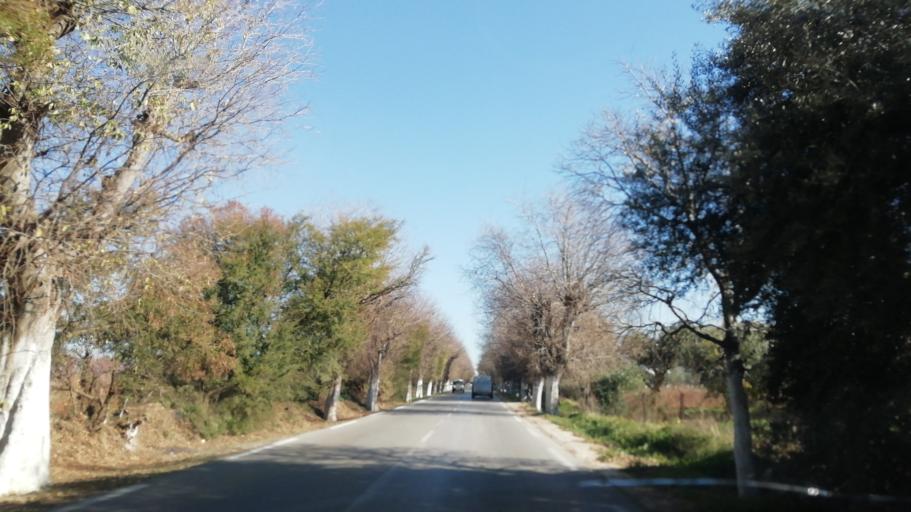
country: DZ
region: Tlemcen
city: Mansoura
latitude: 34.8636
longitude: -1.3676
